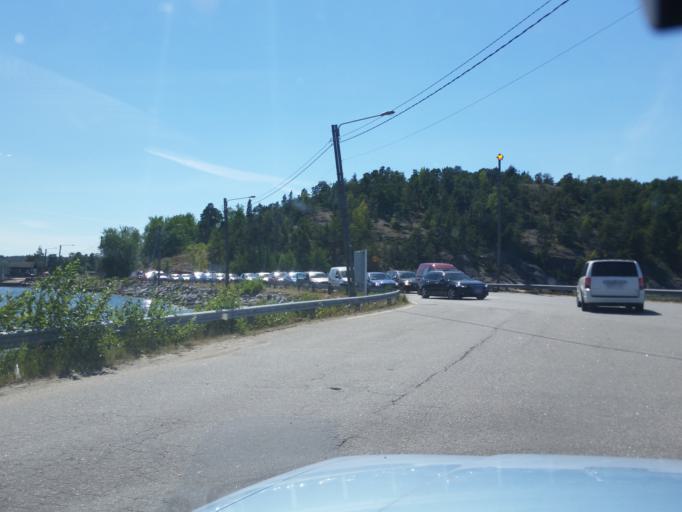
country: FI
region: Varsinais-Suomi
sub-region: Aboland-Turunmaa
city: Nagu
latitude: 60.2222
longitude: 22.0976
